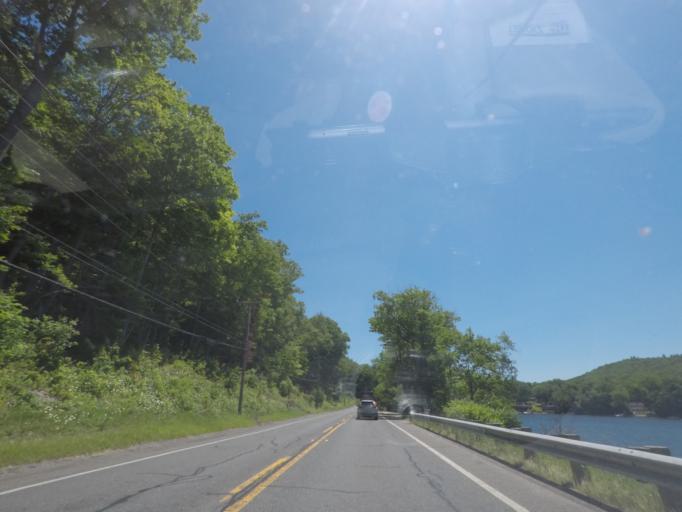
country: US
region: Massachusetts
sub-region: Berkshire County
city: Becket
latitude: 42.2844
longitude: -73.1453
